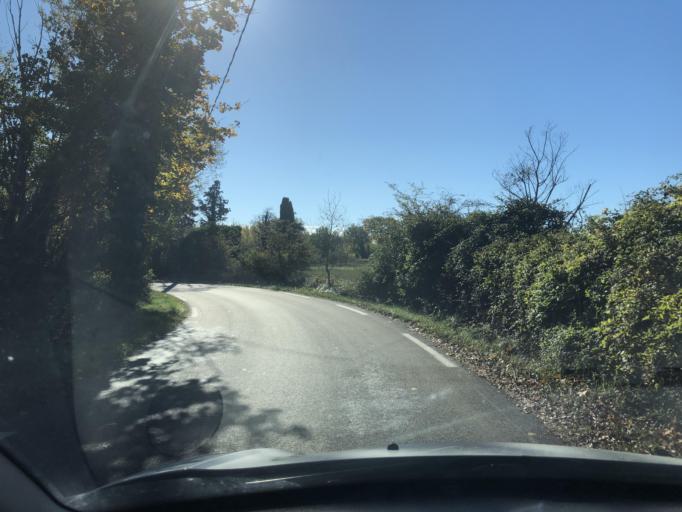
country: FR
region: Provence-Alpes-Cote d'Azur
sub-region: Departement du Vaucluse
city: Althen-des-Paluds
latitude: 43.9801
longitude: 4.9423
